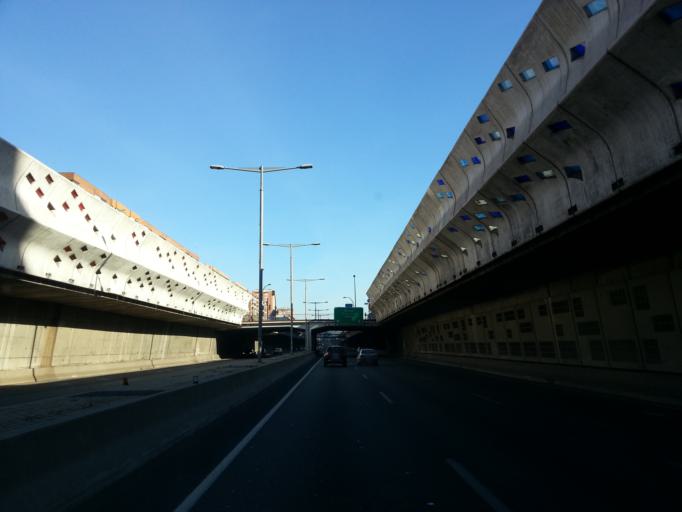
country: ES
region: Catalonia
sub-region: Provincia de Barcelona
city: Sant Marti
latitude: 41.4163
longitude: 2.2042
